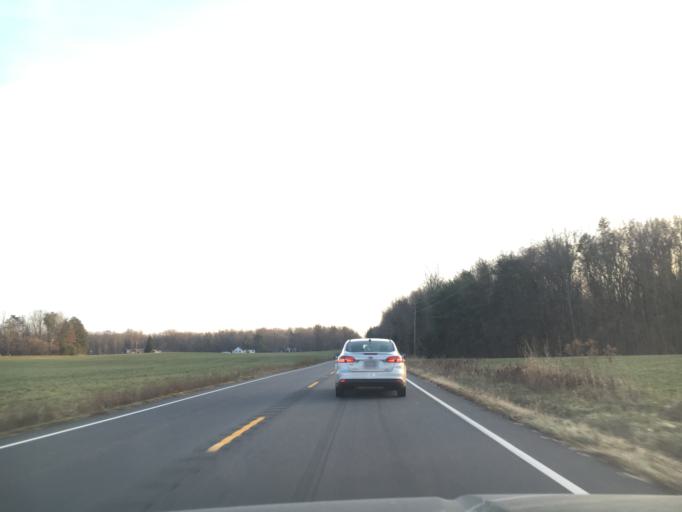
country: US
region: Virginia
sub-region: Culpeper County
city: Culpeper
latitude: 38.3319
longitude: -77.9558
